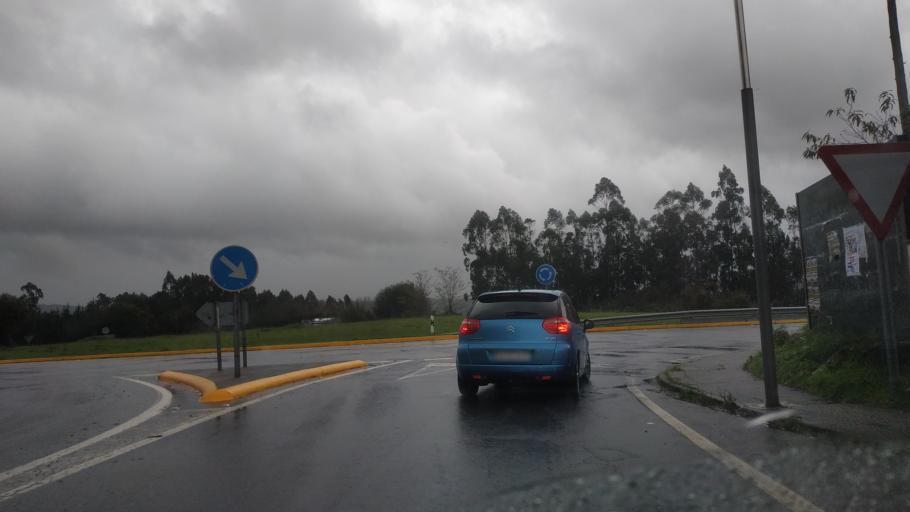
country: ES
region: Galicia
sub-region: Provincia da Coruna
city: Negreira
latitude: 42.9208
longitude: -8.7342
